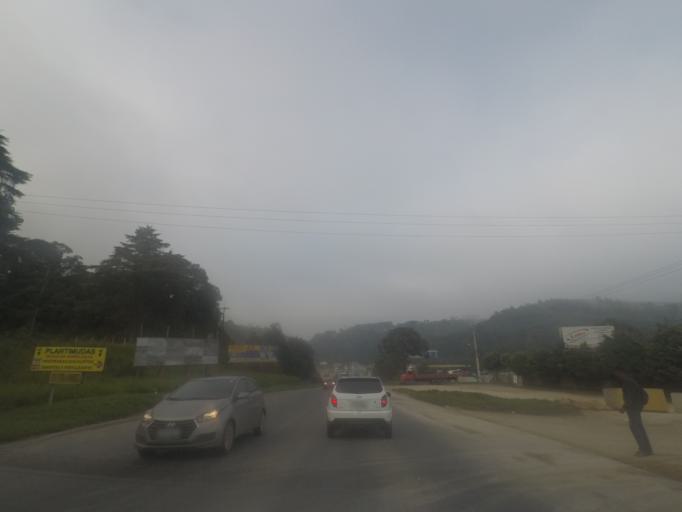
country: BR
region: Parana
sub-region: Almirante Tamandare
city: Almirante Tamandare
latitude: -25.3017
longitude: -49.3038
